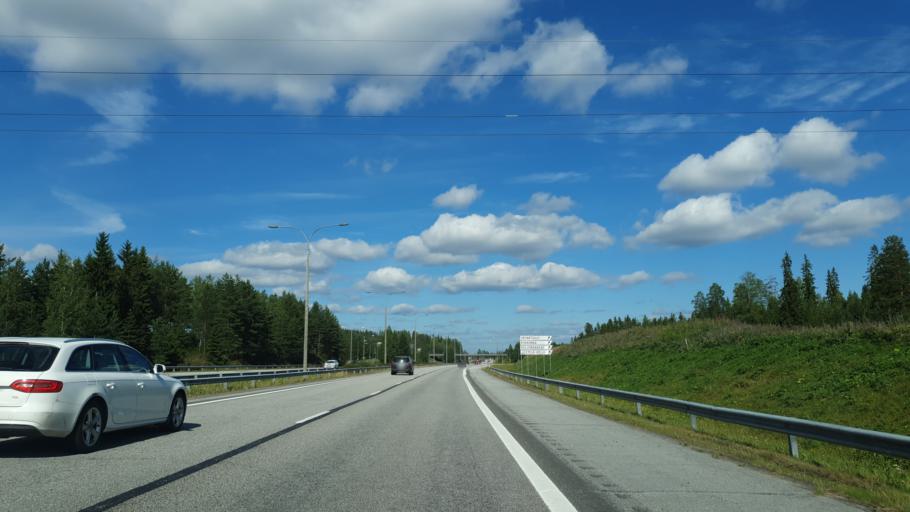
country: FI
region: Central Finland
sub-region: Jyvaeskylae
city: Muurame
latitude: 62.1854
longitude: 25.6882
